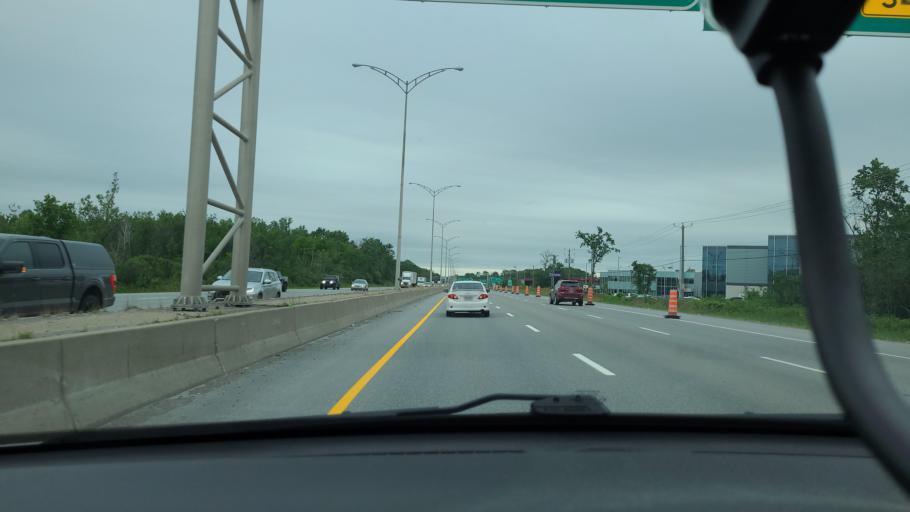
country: CA
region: Quebec
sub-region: Lanaudiere
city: Terrebonne
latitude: 45.6349
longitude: -73.6541
